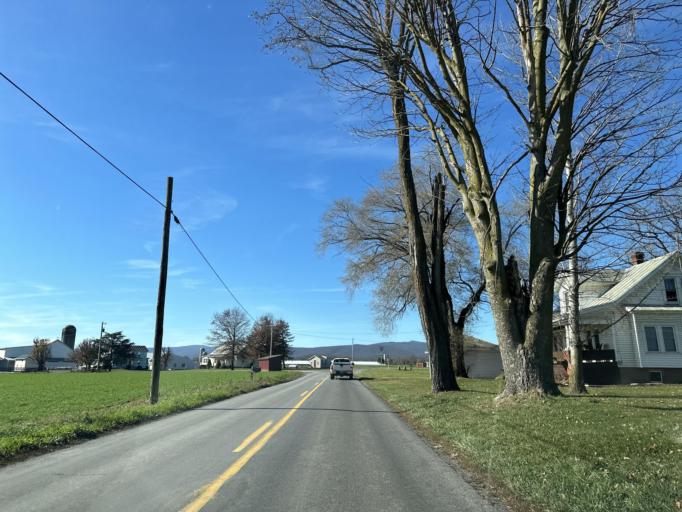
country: US
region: Virginia
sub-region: Rockingham County
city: Bridgewater
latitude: 38.4483
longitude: -79.0051
